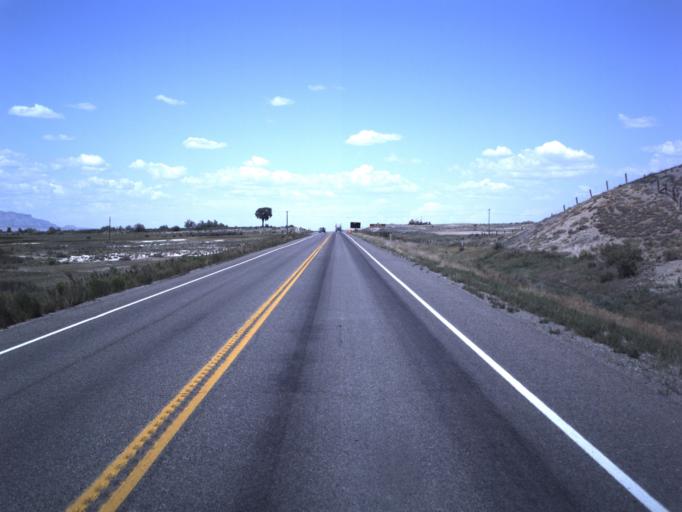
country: US
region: Utah
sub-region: Emery County
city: Castle Dale
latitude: 39.2168
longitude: -110.9991
